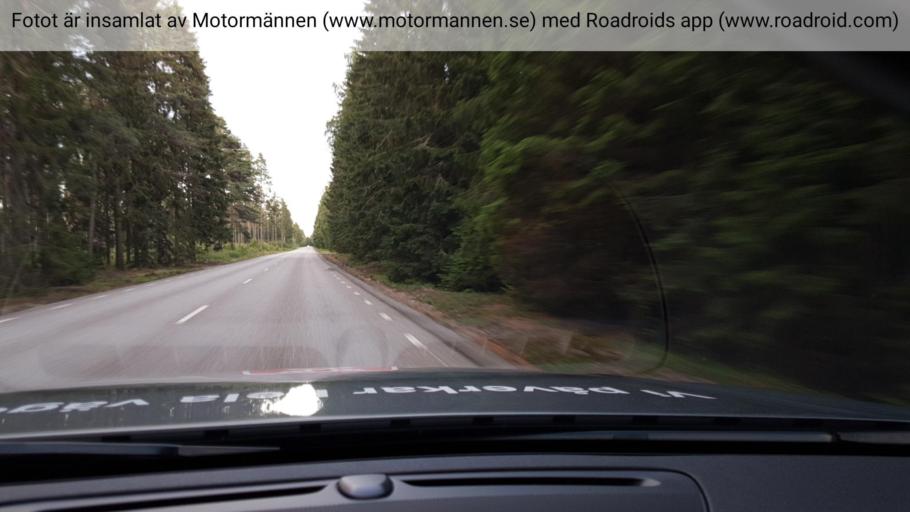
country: SE
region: Vaestmanland
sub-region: Sala Kommun
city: Sala
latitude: 59.8417
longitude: 16.4938
